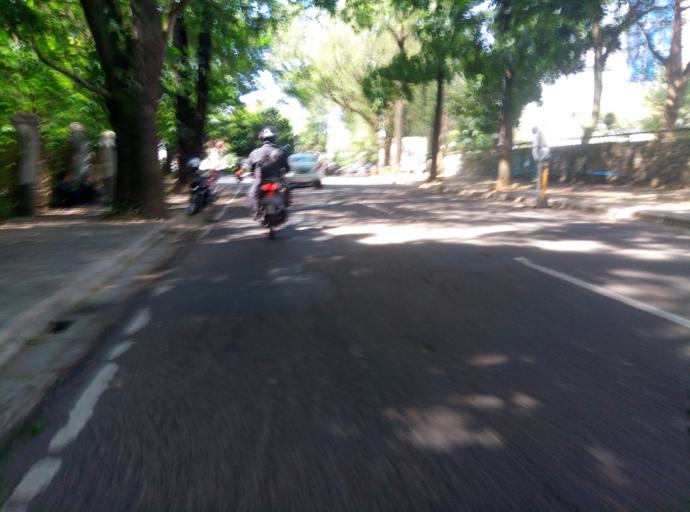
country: ID
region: West Java
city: Bandung
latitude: -6.8875
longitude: 107.6107
